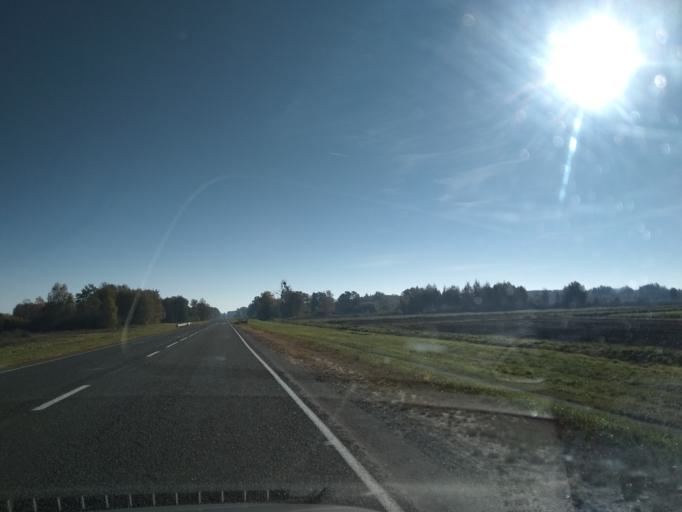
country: BY
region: Brest
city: Malaryta
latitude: 51.8323
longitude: 24.2698
